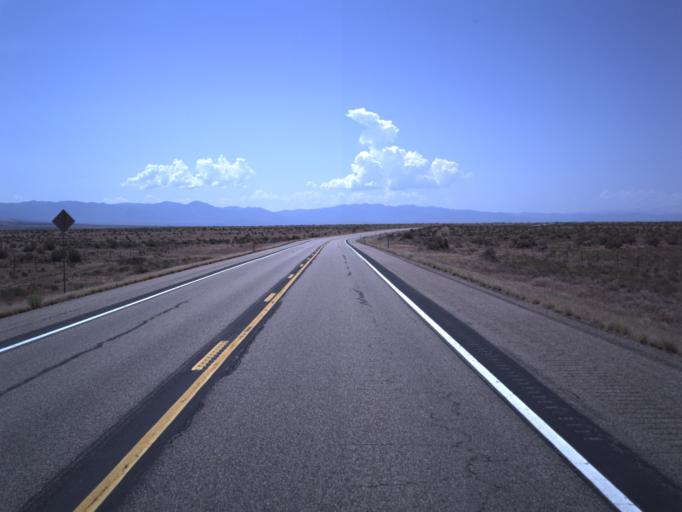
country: US
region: Utah
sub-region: Millard County
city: Delta
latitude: 39.3883
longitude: -112.4987
